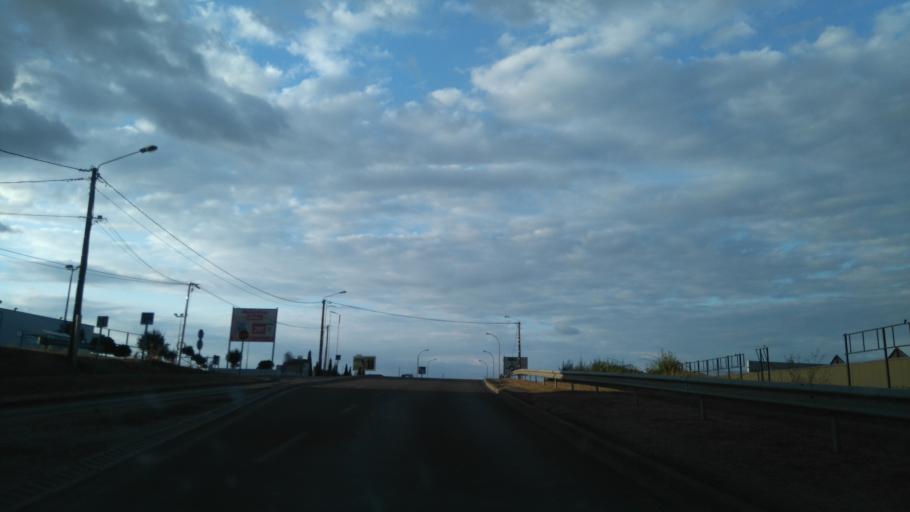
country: FR
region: Poitou-Charentes
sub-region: Departement de la Charente
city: Gond-Pontouvre
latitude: 45.6878
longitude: 0.1789
